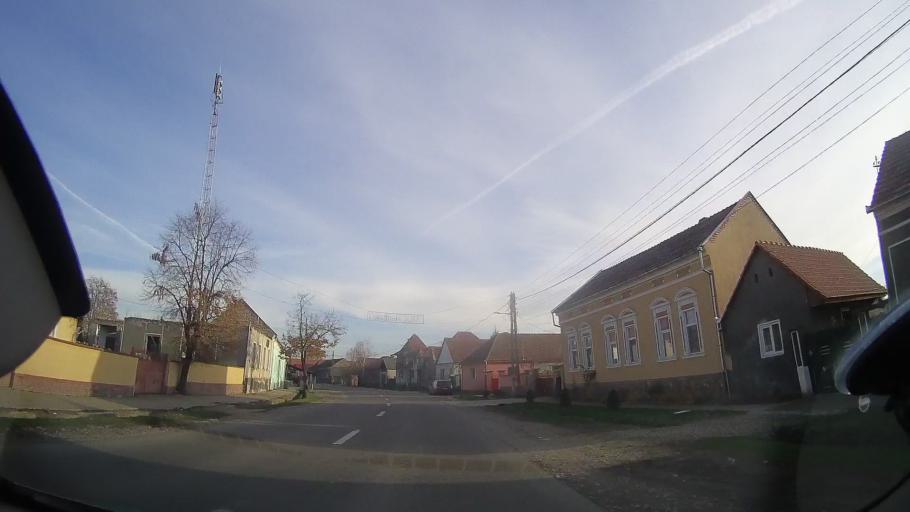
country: RO
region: Bihor
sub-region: Comuna Tetchea
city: Hotar
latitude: 47.0545
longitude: 22.2765
